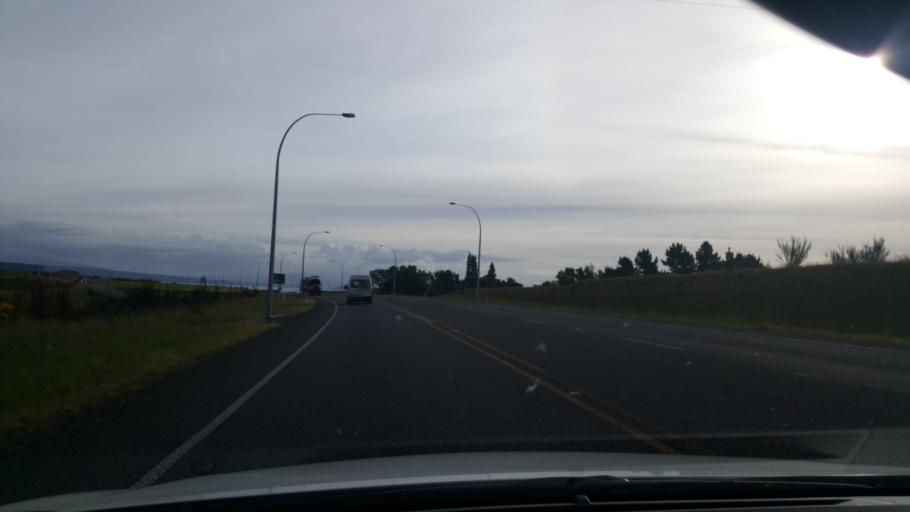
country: NZ
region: Waikato
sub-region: Taupo District
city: Taupo
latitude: -38.7358
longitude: 176.0754
